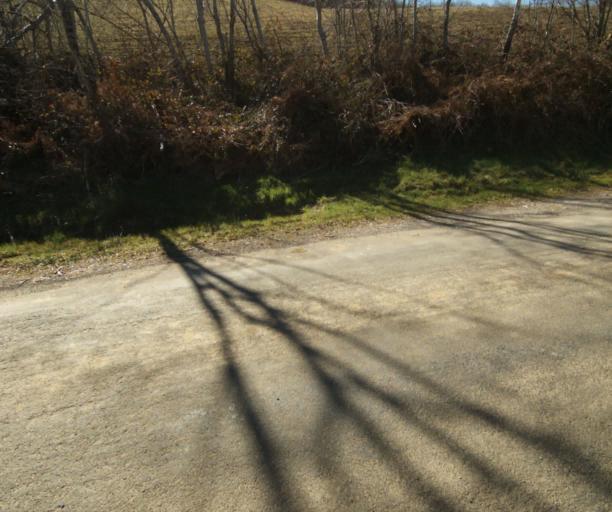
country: FR
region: Limousin
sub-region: Departement de la Correze
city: Chamboulive
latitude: 45.4490
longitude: 1.6812
